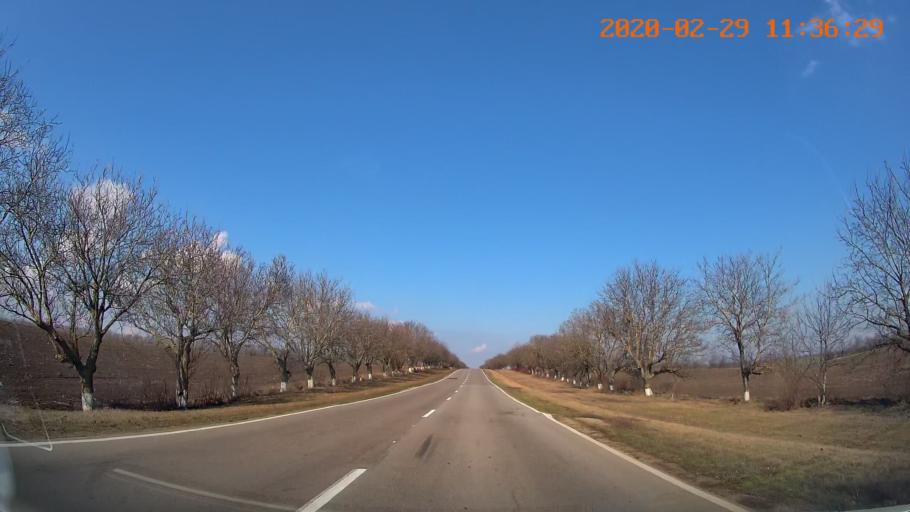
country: MD
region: Rezina
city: Saharna
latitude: 47.5967
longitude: 29.0553
